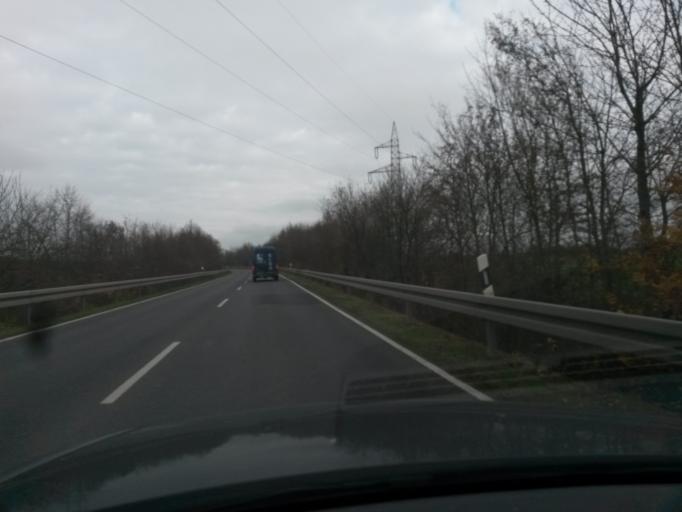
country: DE
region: Bavaria
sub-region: Regierungsbezirk Unterfranken
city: Estenfeld
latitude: 49.8317
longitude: 9.9882
